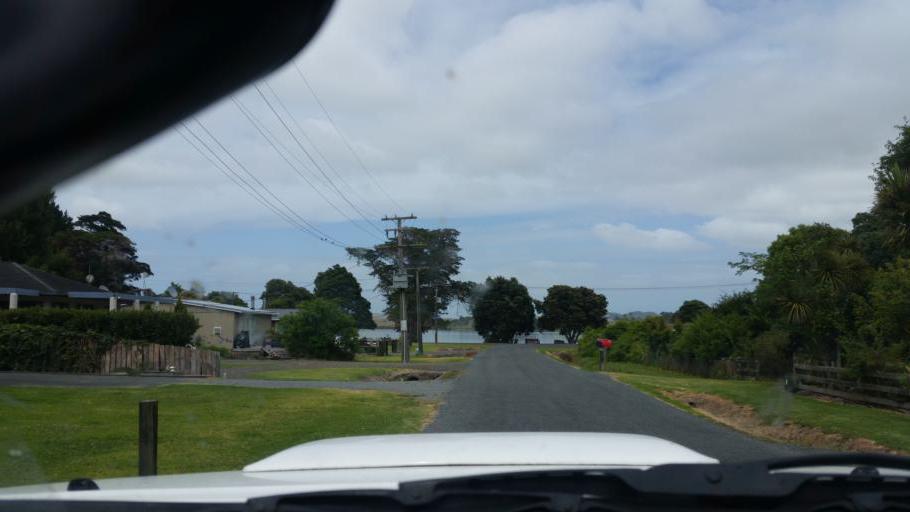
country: NZ
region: Auckland
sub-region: Auckland
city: Wellsford
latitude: -36.1584
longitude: 174.2383
